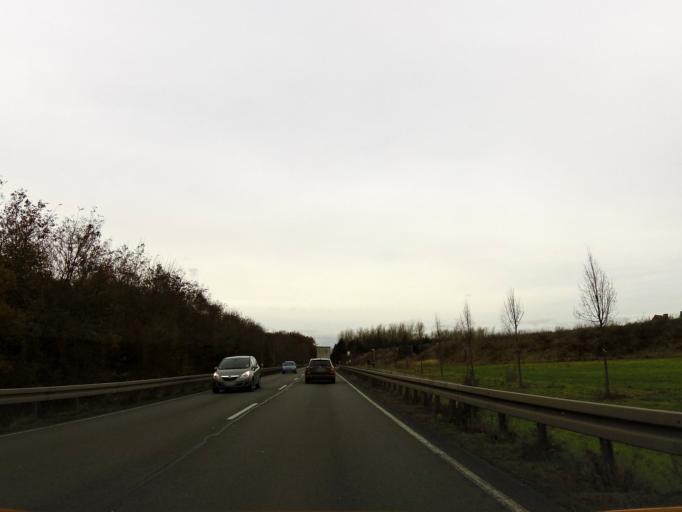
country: DE
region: Saxony-Anhalt
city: Salzwedel
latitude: 52.8350
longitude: 11.1819
